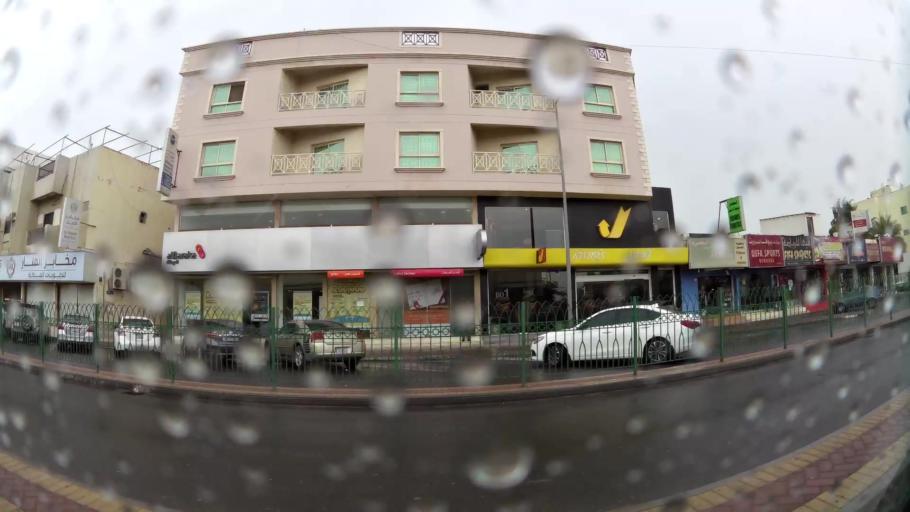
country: BH
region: Northern
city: Madinat `Isa
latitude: 26.1759
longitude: 50.5559
